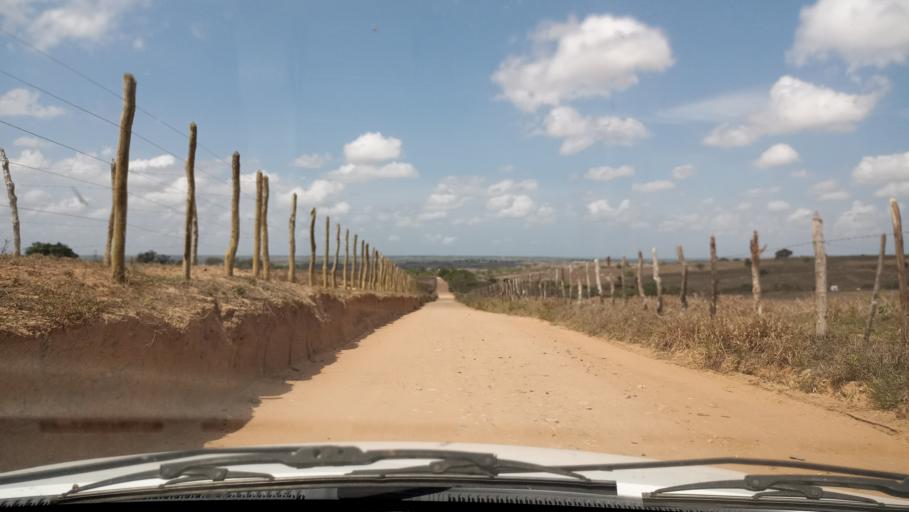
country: BR
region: Rio Grande do Norte
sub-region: Pedro Velho
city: Pedro Velho
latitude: -6.3469
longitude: -35.3300
